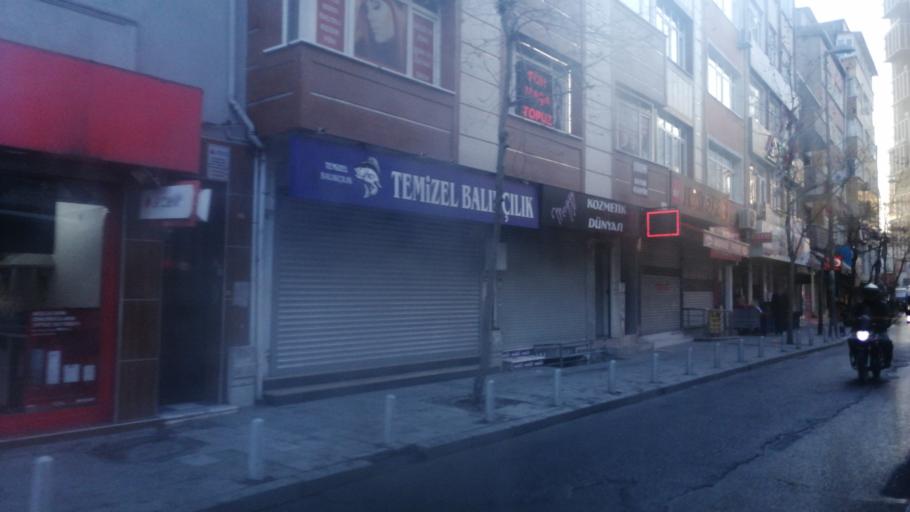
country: TR
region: Istanbul
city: Sisli
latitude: 41.0797
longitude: 28.9946
